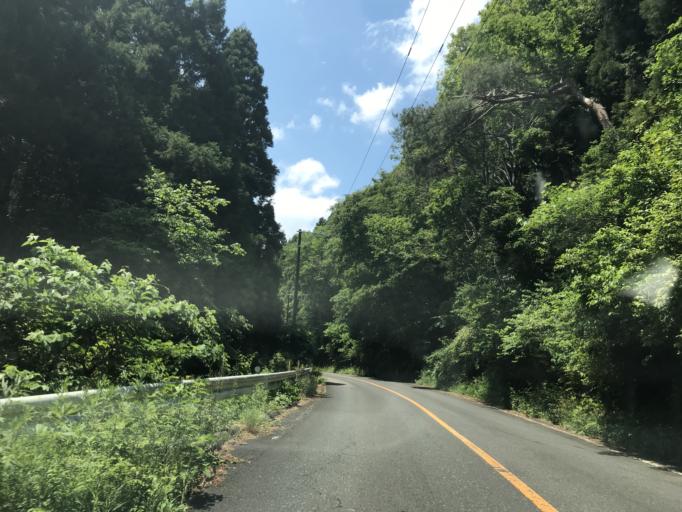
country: JP
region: Miyagi
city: Matsushima
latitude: 38.3634
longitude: 141.0500
